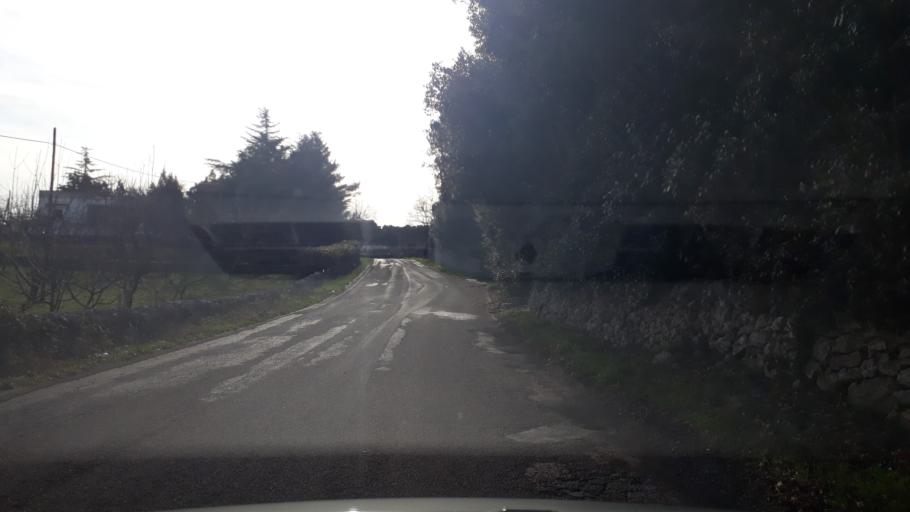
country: IT
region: Apulia
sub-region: Provincia di Taranto
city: Martina Franca
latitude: 40.6742
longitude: 17.3625
